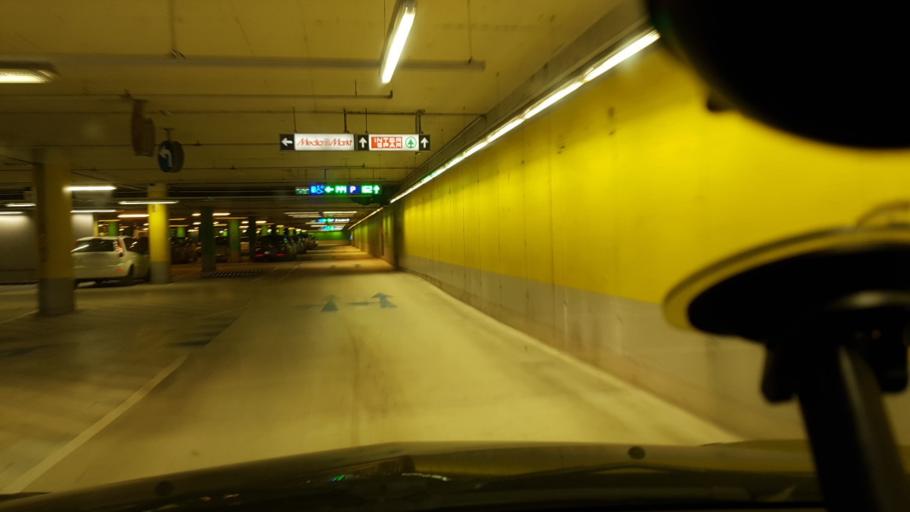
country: AT
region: Lower Austria
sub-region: Politischer Bezirk Wiener Neustadt
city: Theresienfeld
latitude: 47.8200
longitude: 16.2181
